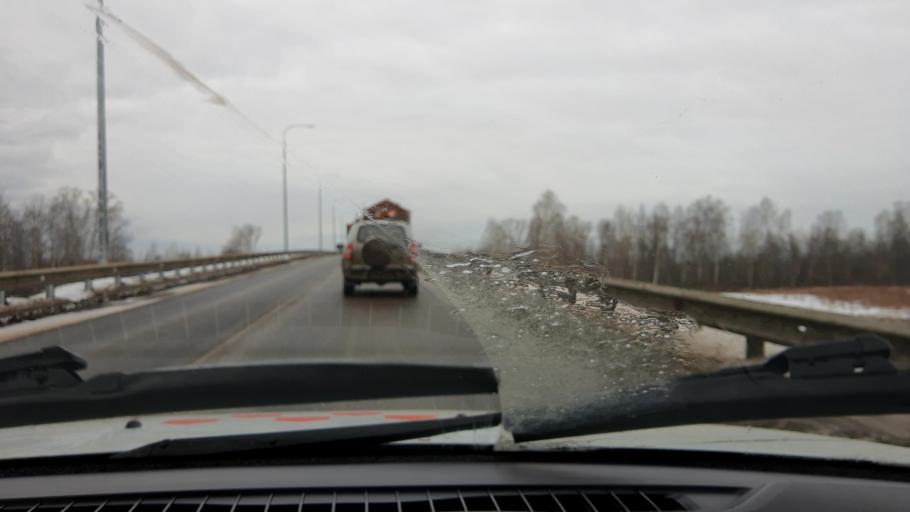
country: RU
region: Nizjnij Novgorod
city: Neklyudovo
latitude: 56.4230
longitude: 43.9865
